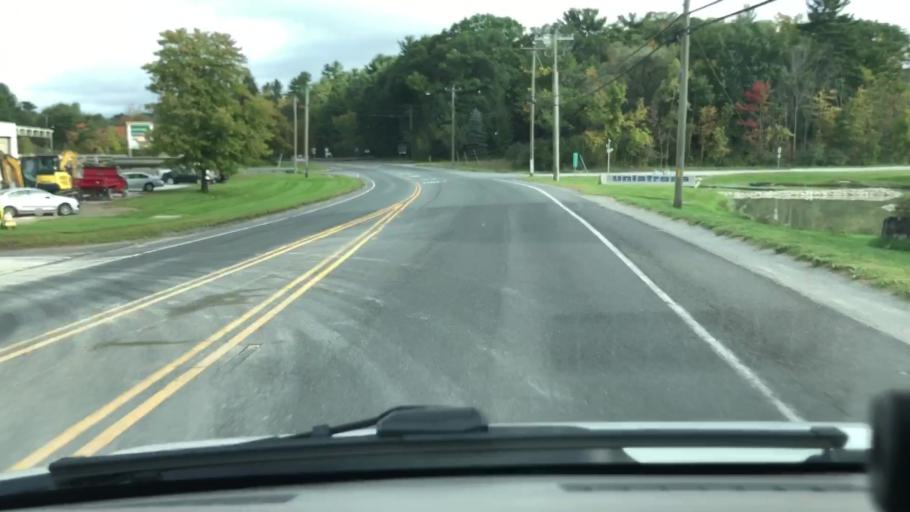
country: US
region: Massachusetts
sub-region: Berkshire County
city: Dalton
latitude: 42.4863
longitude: -73.2020
